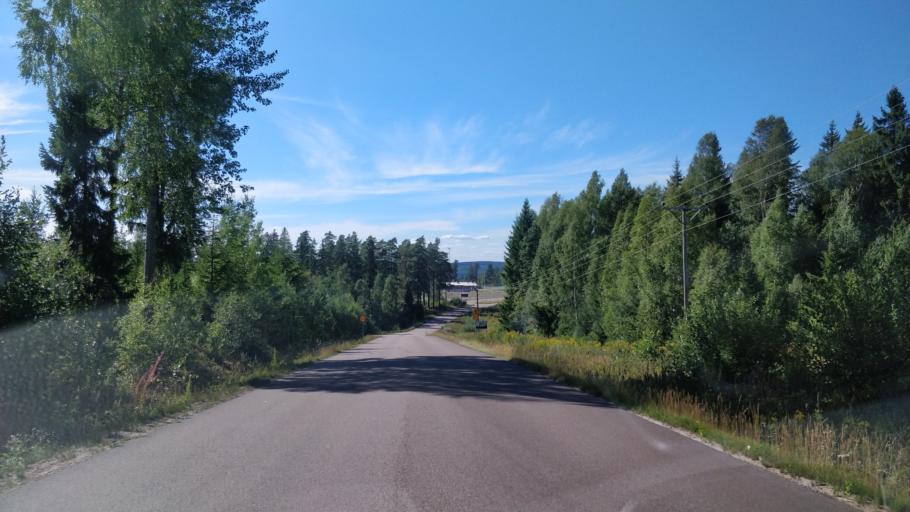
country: SE
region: Vaermland
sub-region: Hagfors Kommun
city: Hagfors
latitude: 60.0382
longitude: 13.7252
